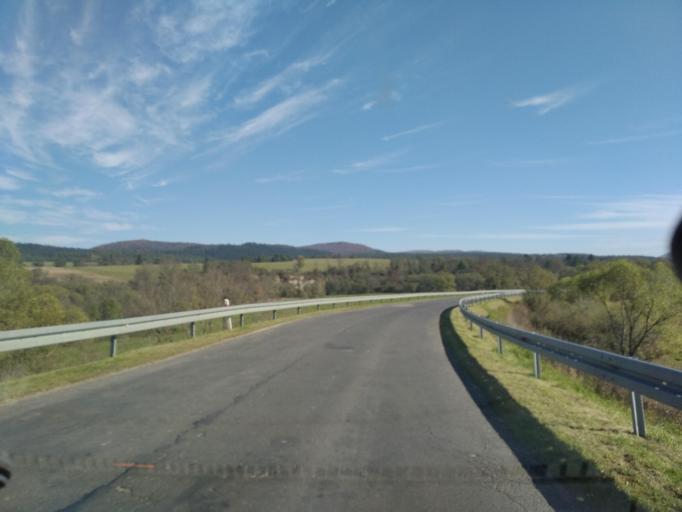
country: PL
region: Subcarpathian Voivodeship
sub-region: Powiat sanocki
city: Komancza
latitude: 49.2489
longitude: 22.1215
